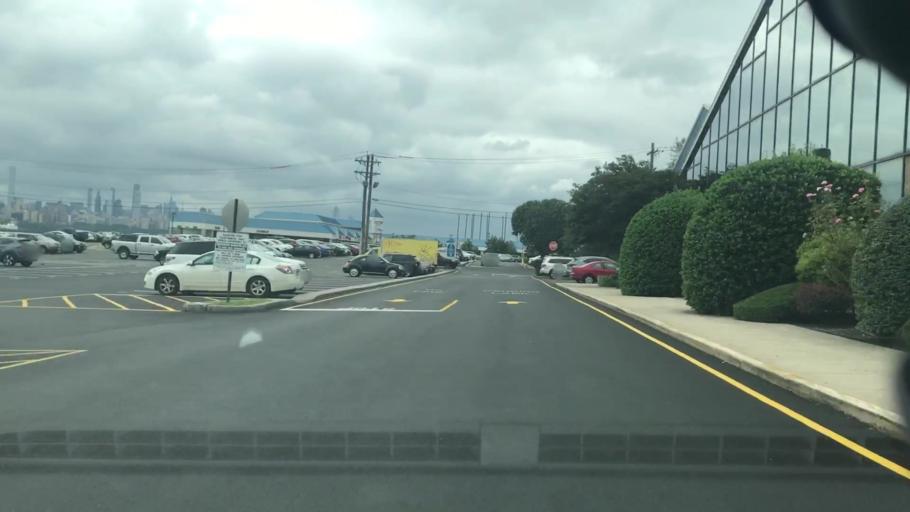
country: US
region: New Jersey
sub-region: Bergen County
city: Edgewater
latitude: 40.8209
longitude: -73.9762
